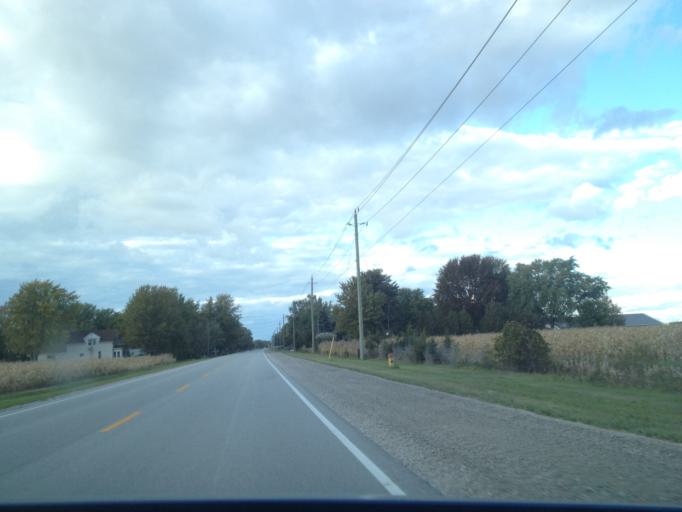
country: US
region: Michigan
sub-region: Wayne County
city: Grosse Pointe Farms
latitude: 42.2609
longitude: -82.7135
